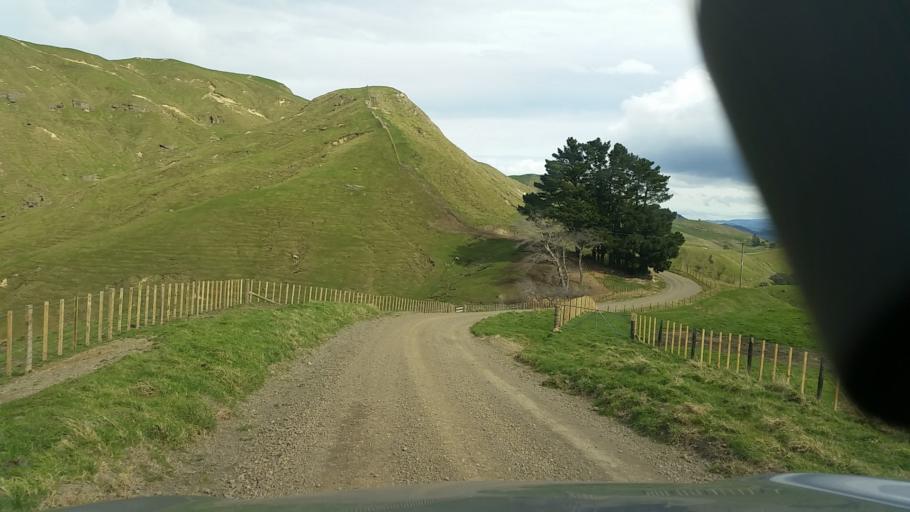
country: NZ
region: Hawke's Bay
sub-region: Napier City
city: Napier
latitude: -39.2039
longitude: 176.9416
